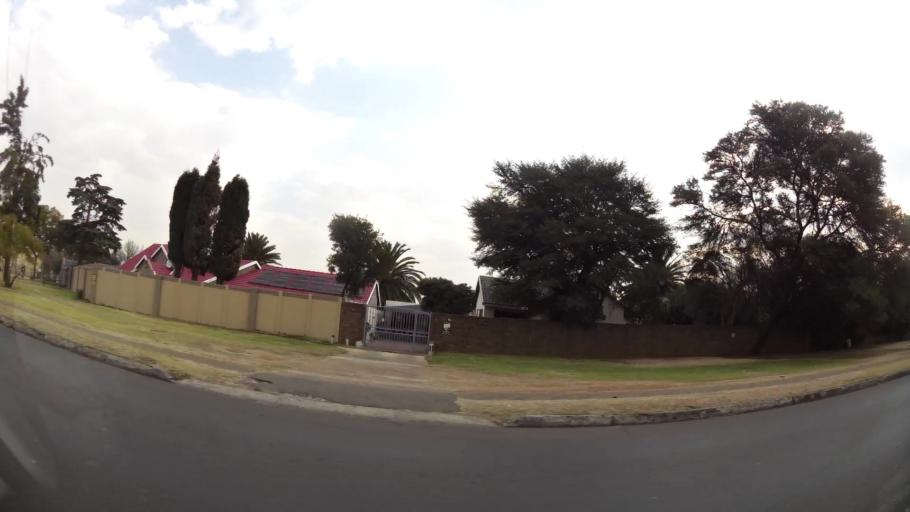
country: ZA
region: Gauteng
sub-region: City of Johannesburg Metropolitan Municipality
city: Modderfontein
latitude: -26.1383
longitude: 28.1831
